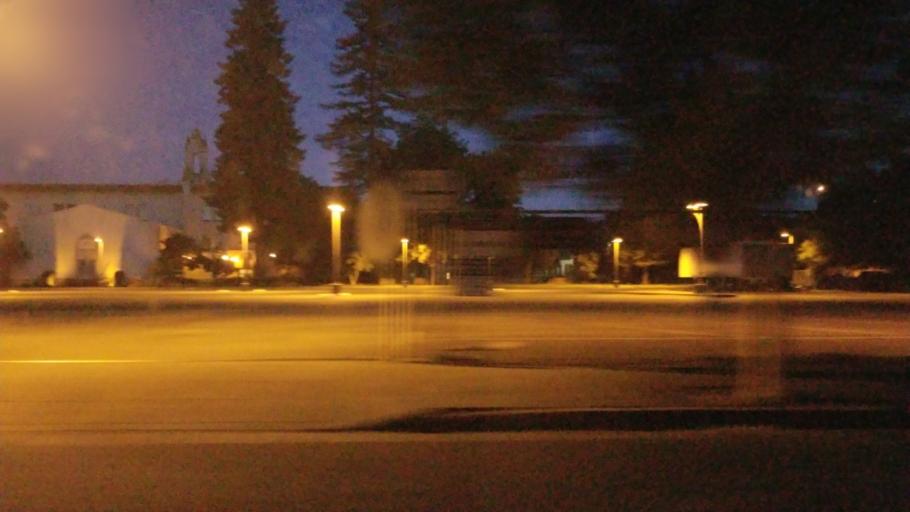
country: US
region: California
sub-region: Sonoma County
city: Santa Rosa
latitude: 38.4438
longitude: -122.7207
